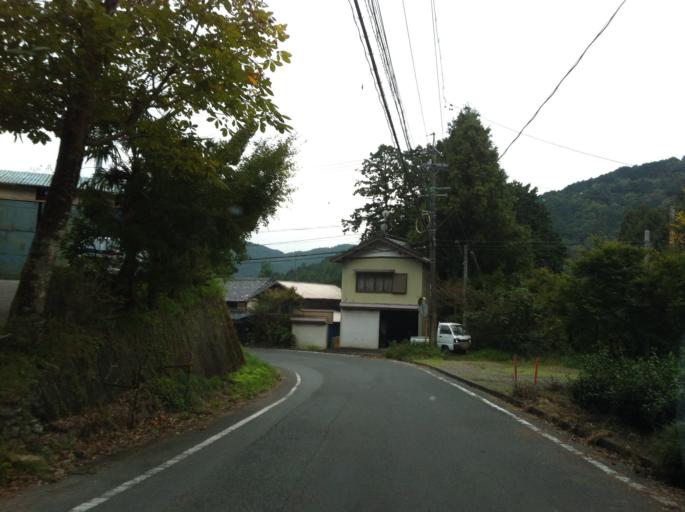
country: JP
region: Shizuoka
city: Mori
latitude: 34.8560
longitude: 138.0147
